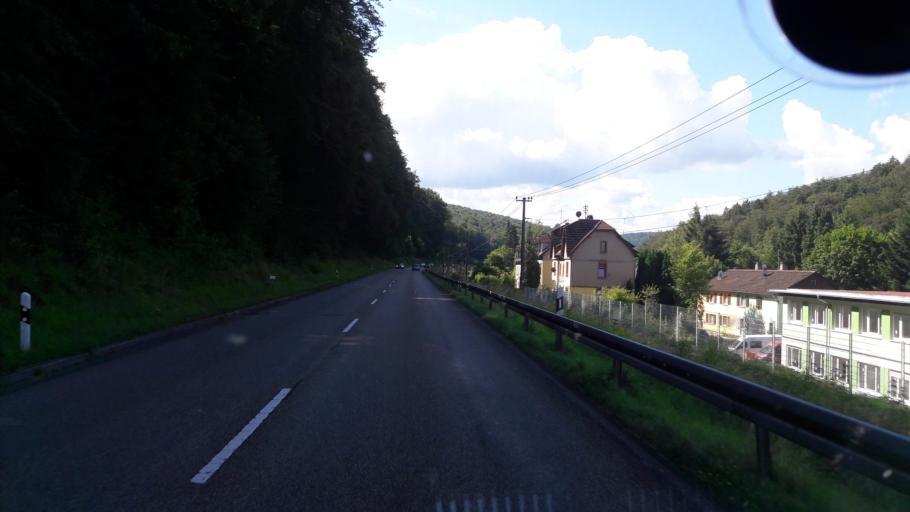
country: DE
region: Baden-Wuerttemberg
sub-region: Karlsruhe Region
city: Ettlingen
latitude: 48.9085
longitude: 8.4544
